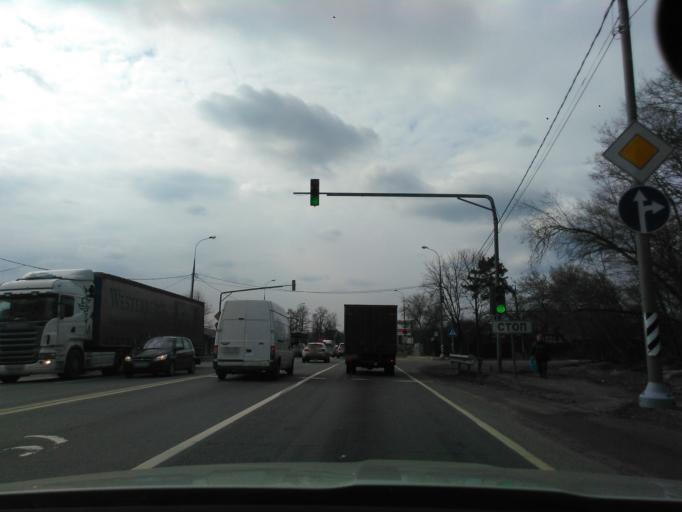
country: RU
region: Moskovskaya
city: Marfino
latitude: 56.0117
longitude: 37.5455
